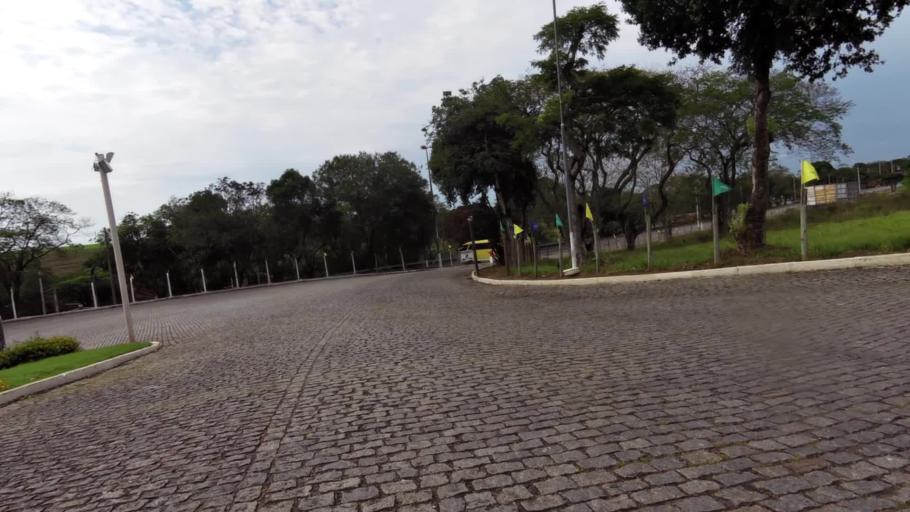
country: BR
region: Rio de Janeiro
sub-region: Campos Dos Goytacazes
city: Campos
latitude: -21.8354
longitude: -41.4377
